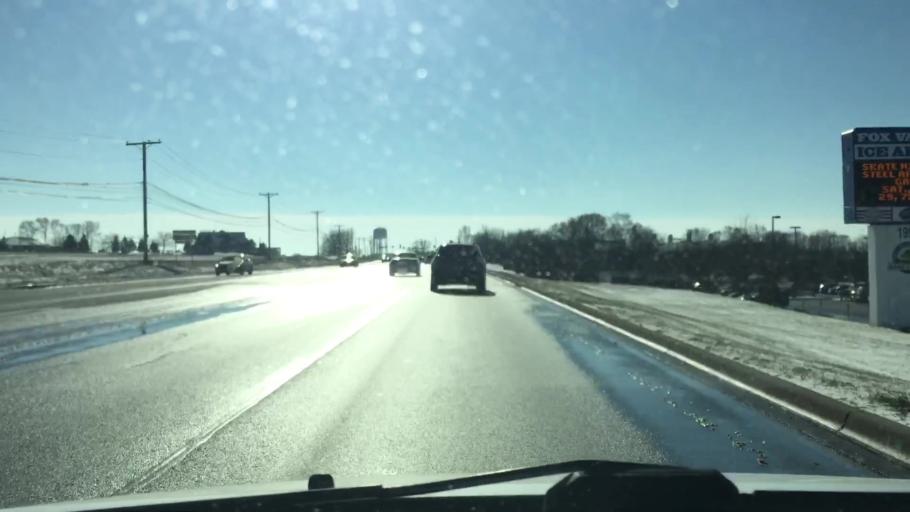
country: US
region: Illinois
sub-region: Kane County
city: Geneva
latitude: 41.8732
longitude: -88.2788
